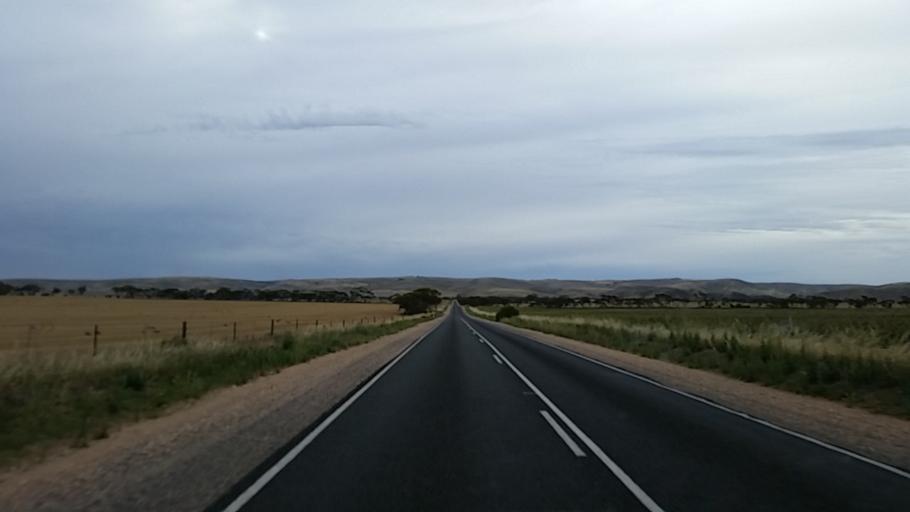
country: AU
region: South Australia
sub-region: Mid Murray
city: Mannum
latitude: -34.7555
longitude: 139.2501
